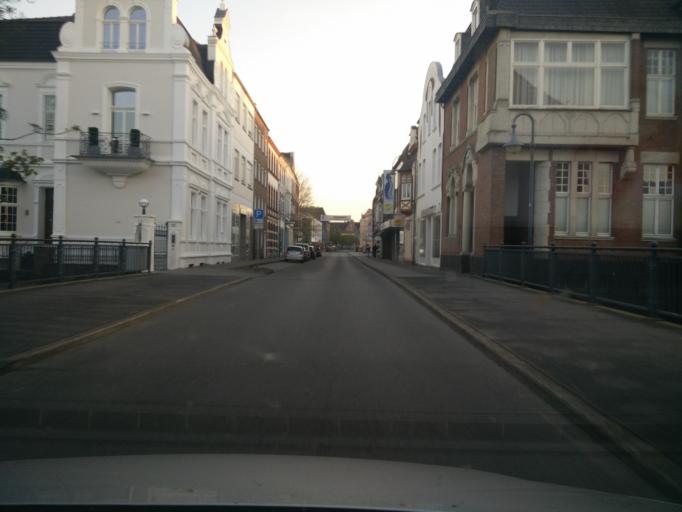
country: DE
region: North Rhine-Westphalia
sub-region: Regierungsbezirk Dusseldorf
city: Goch
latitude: 51.6781
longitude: 6.1575
